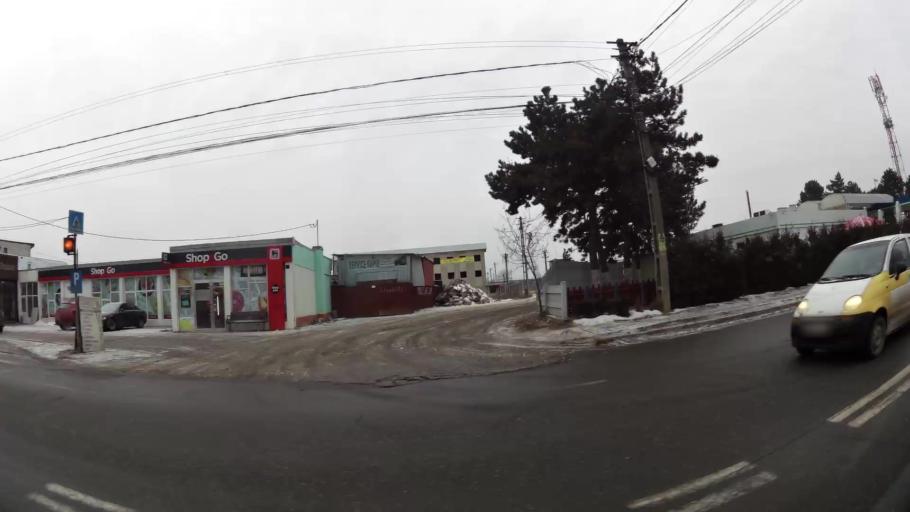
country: RO
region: Dambovita
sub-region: Comuna Ulmi
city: Ulmi
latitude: 44.9105
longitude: 25.4870
